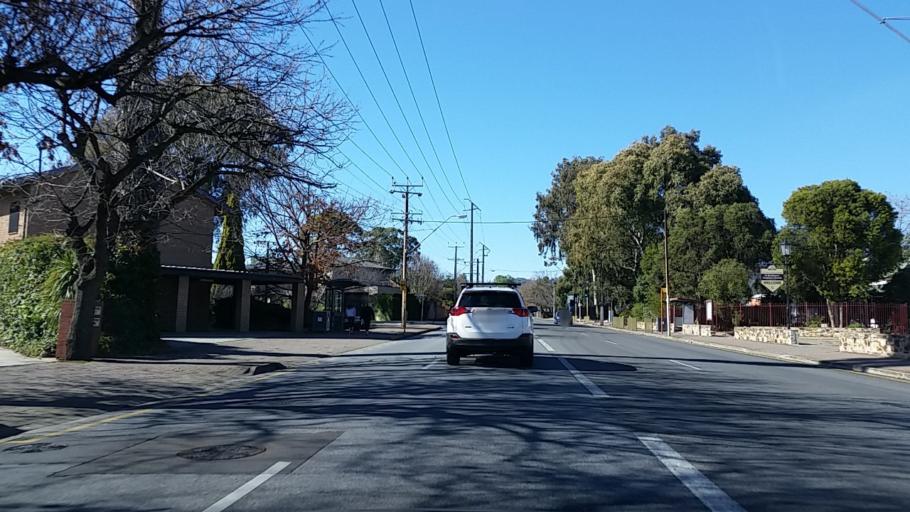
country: AU
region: South Australia
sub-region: Norwood Payneham St Peters
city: Trinity Gardens
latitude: -34.9268
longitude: 138.6441
